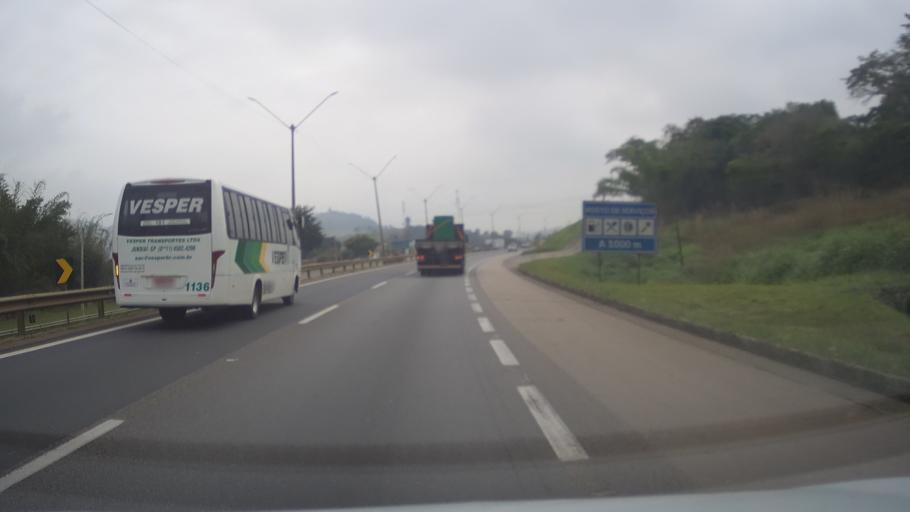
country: BR
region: Sao Paulo
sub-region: Atibaia
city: Atibaia
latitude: -23.0380
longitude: -46.5552
